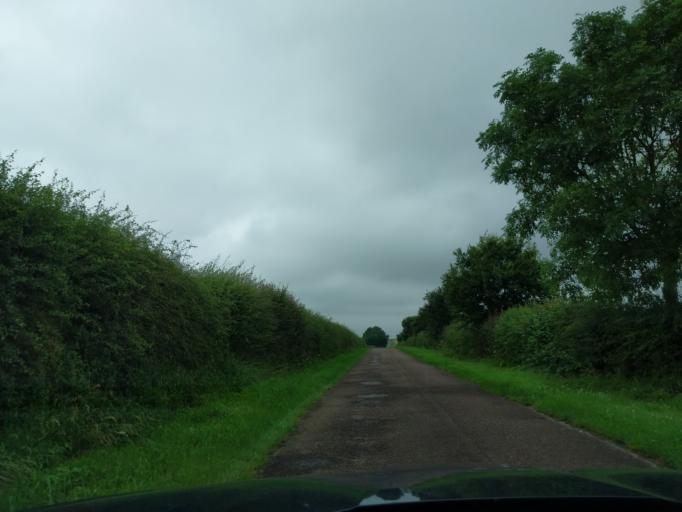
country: GB
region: England
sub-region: Northumberland
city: Ford
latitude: 55.6860
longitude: -2.1262
